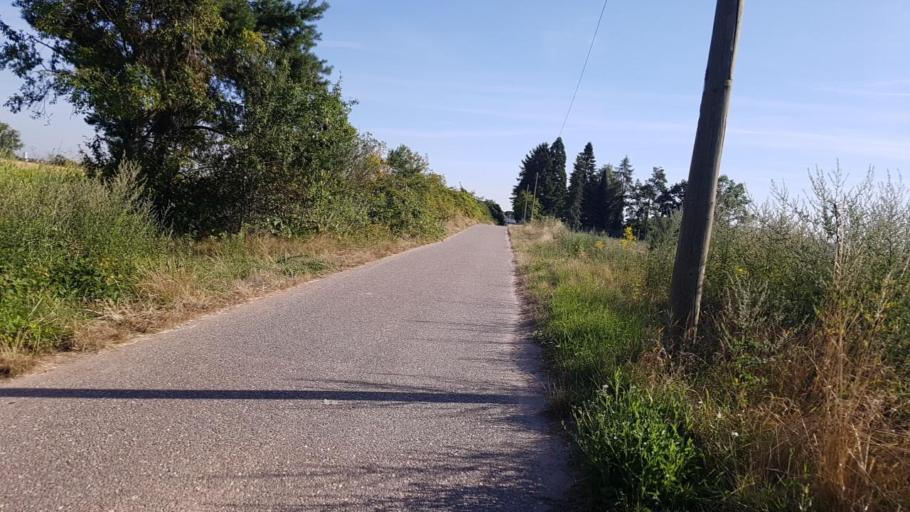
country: DE
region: Baden-Wuerttemberg
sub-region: Karlsruhe Region
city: Reilingen
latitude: 49.2899
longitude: 8.5519
